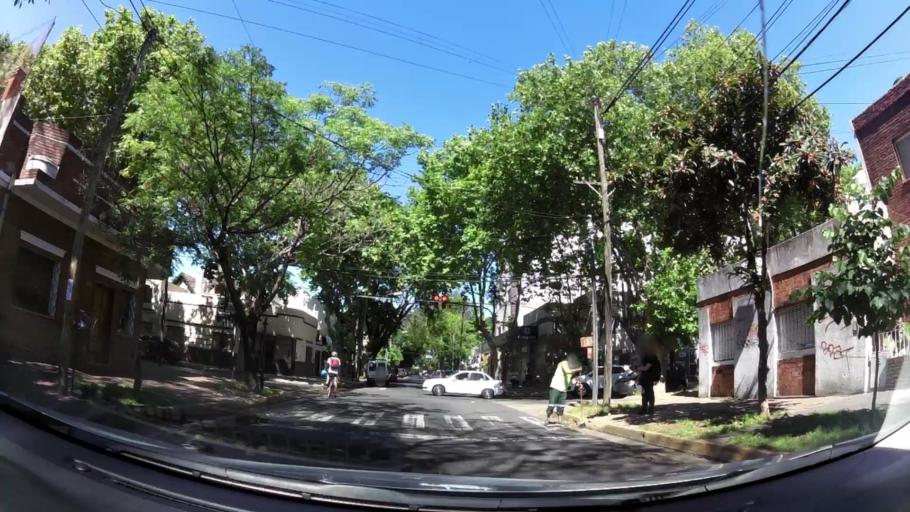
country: AR
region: Buenos Aires
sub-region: Partido de Vicente Lopez
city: Olivos
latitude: -34.5285
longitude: -58.4855
